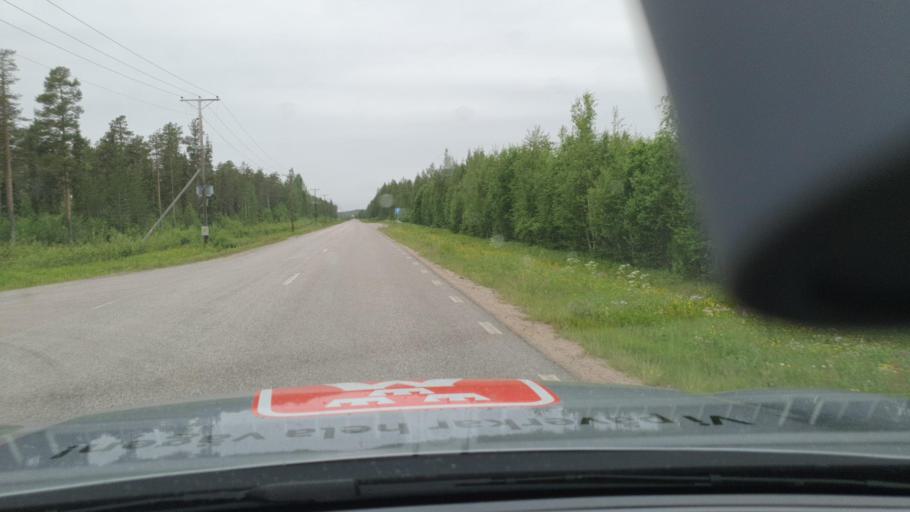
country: SE
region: Norrbotten
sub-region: Overtornea Kommun
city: OEvertornea
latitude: 66.3956
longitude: 23.5942
